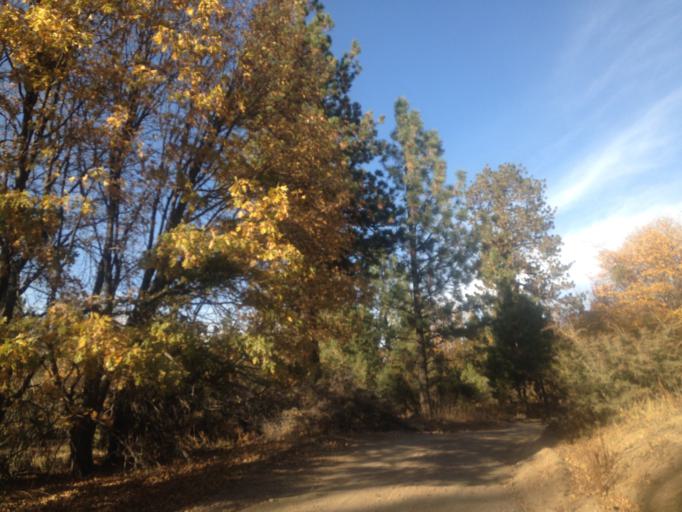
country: US
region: California
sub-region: San Bernardino County
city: Yucaipa
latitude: 34.1332
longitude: -117.0116
